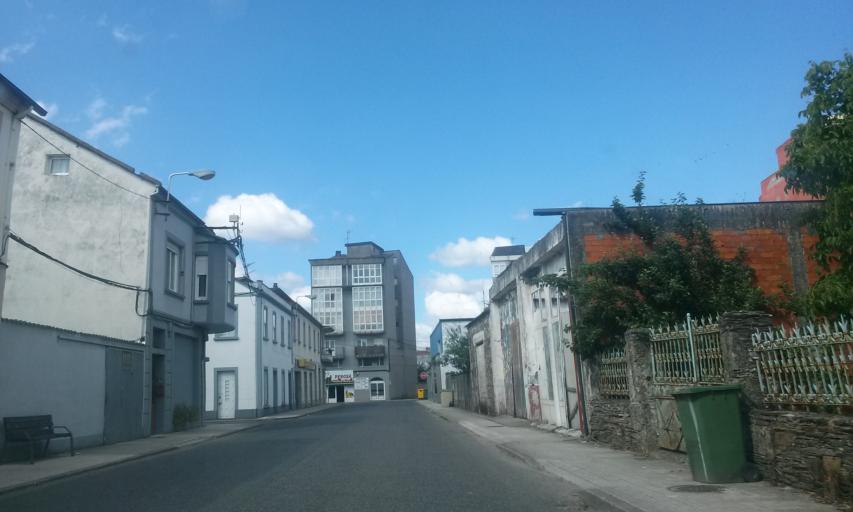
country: ES
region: Galicia
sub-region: Provincia de Lugo
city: Rabade
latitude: 43.1196
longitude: -7.6281
